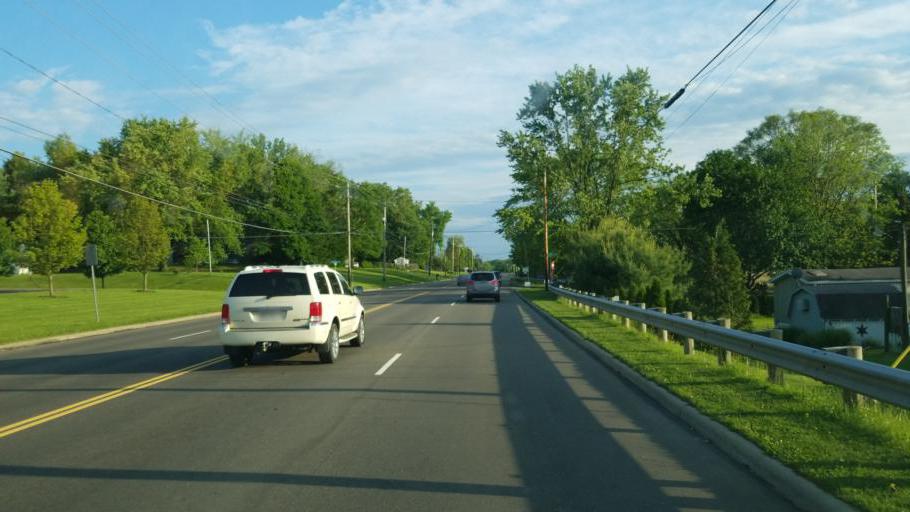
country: US
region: Ohio
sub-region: Stark County
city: Uniontown
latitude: 40.9857
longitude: -81.4060
